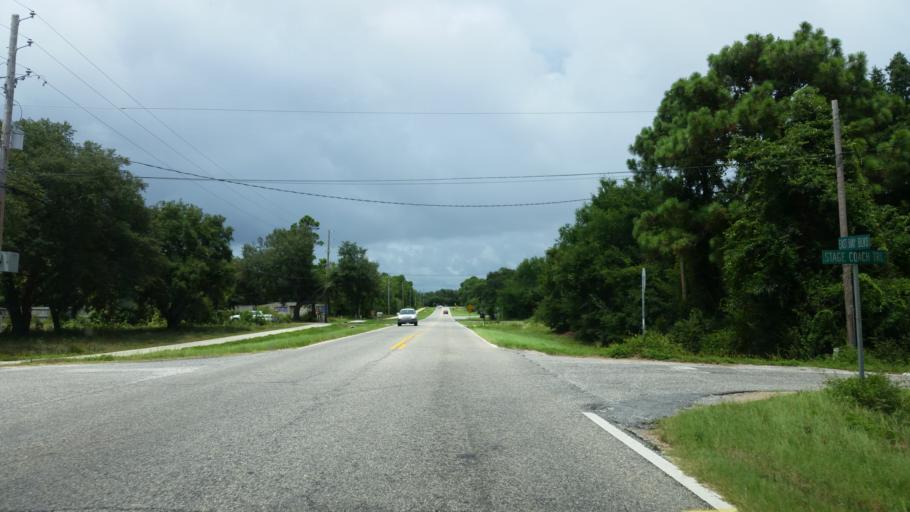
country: US
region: Florida
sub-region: Santa Rosa County
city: Woodlawn Beach
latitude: 30.4034
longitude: -86.9998
